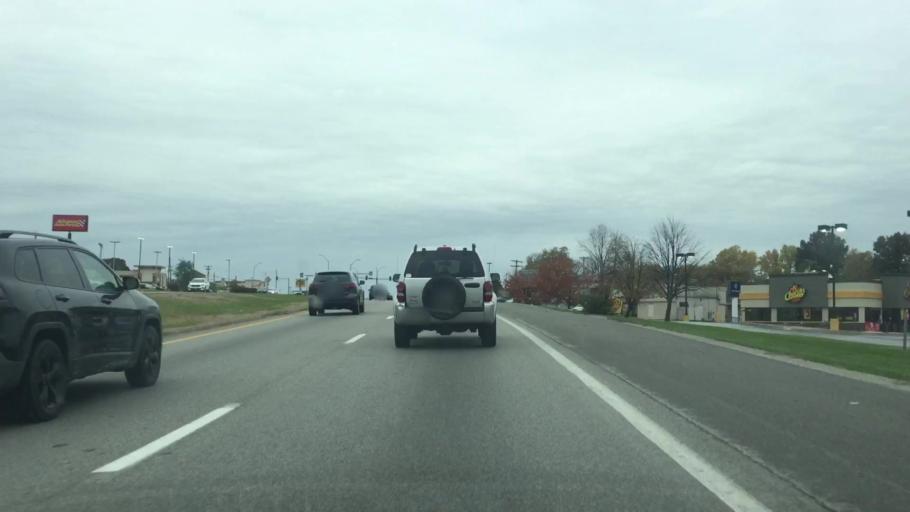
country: US
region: Missouri
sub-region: Jackson County
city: Raytown
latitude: 38.9934
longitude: -94.4713
